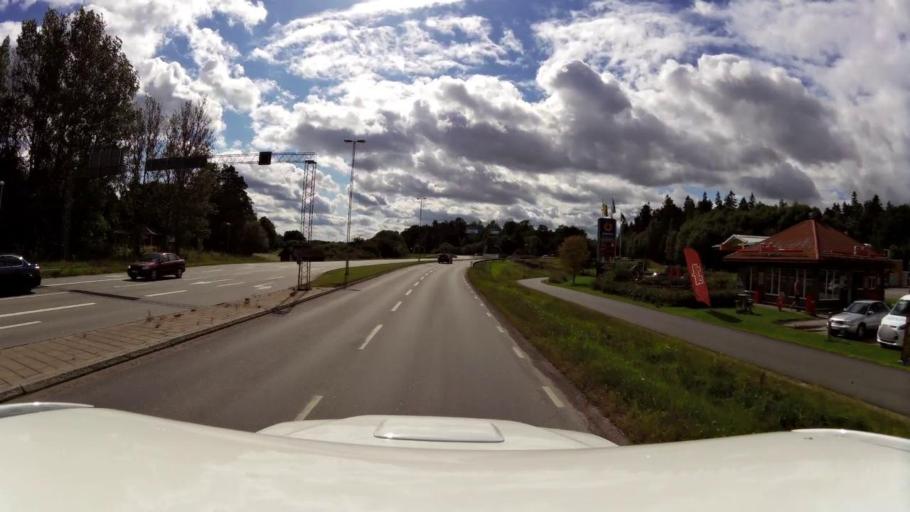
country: SE
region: OEstergoetland
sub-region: Linkopings Kommun
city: Linkoping
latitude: 58.3982
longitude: 15.6072
